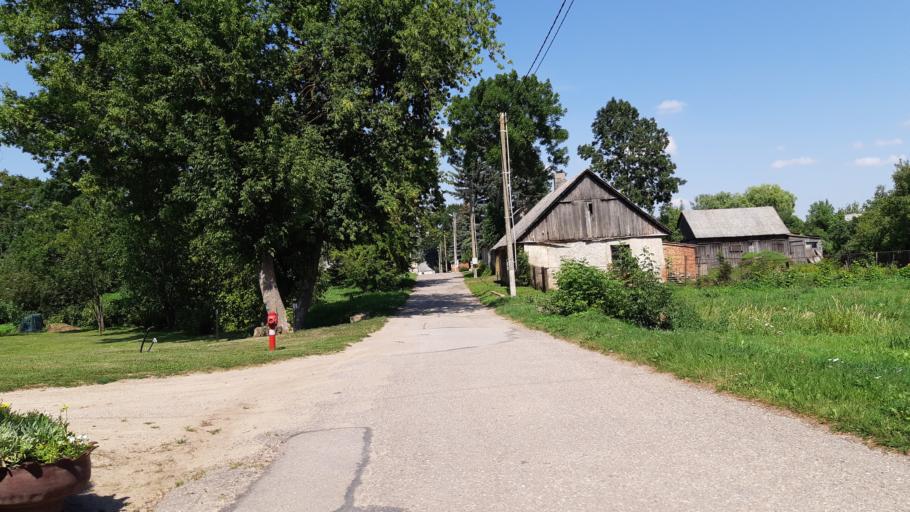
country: LT
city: Virbalis
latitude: 54.6234
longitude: 22.8204
